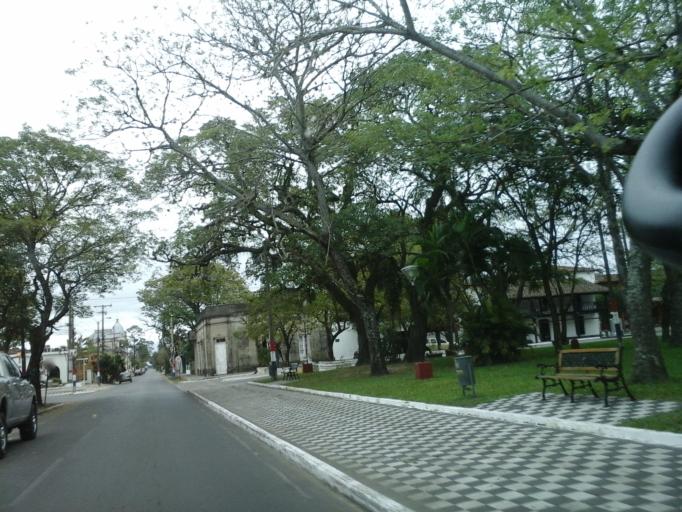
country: PY
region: Neembucu
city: Pilar
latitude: -26.8562
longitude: -58.3051
